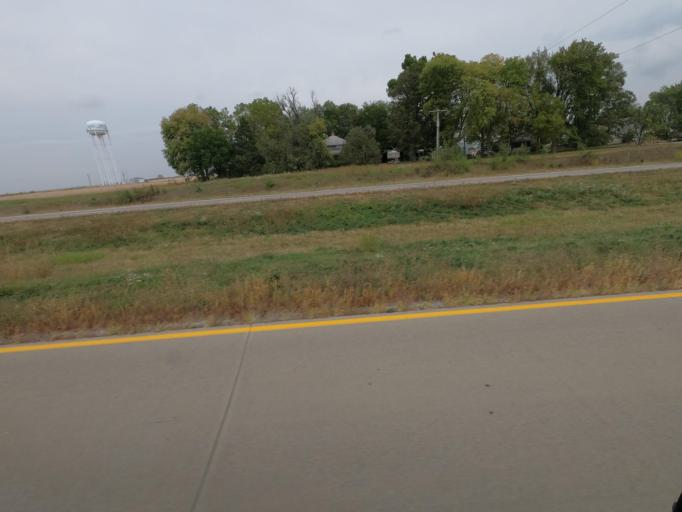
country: US
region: Iowa
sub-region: Mahaska County
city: Oskaloosa
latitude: 41.3324
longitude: -92.7229
